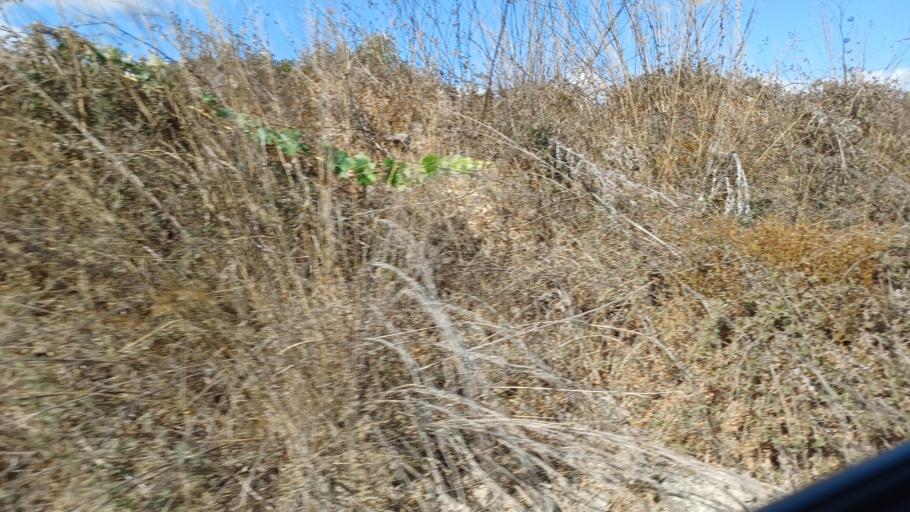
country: CY
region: Pafos
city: Mesogi
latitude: 34.8434
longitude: 32.5305
